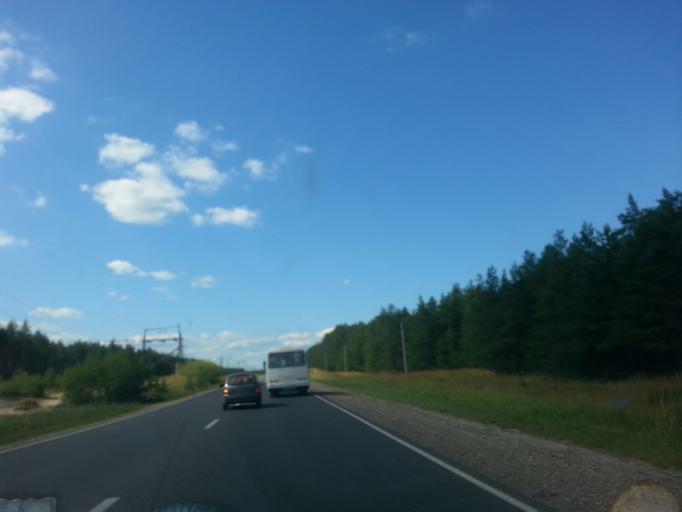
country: RU
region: Nizjnij Novgorod
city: Lukino
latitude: 56.3939
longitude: 43.6837
